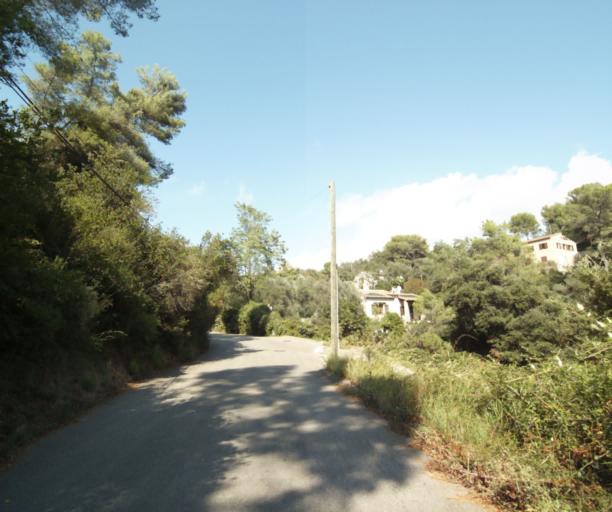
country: FR
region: Provence-Alpes-Cote d'Azur
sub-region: Departement des Alpes-Maritimes
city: Drap
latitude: 43.7558
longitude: 7.3376
